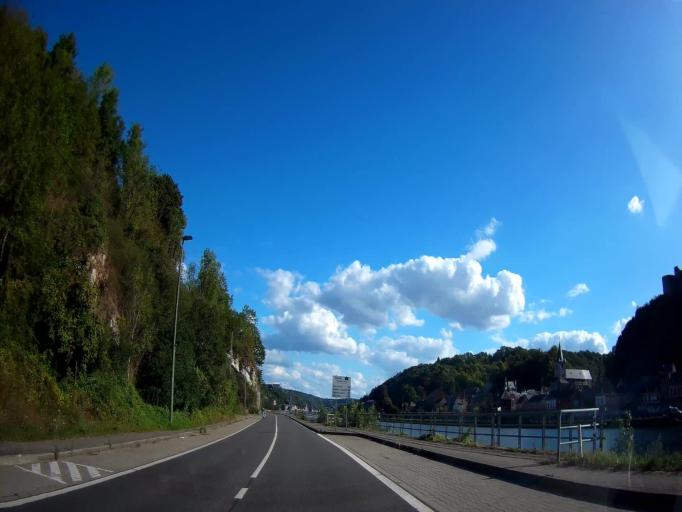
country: BE
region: Wallonia
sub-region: Province de Namur
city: Dinant
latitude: 50.2760
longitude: 4.8981
